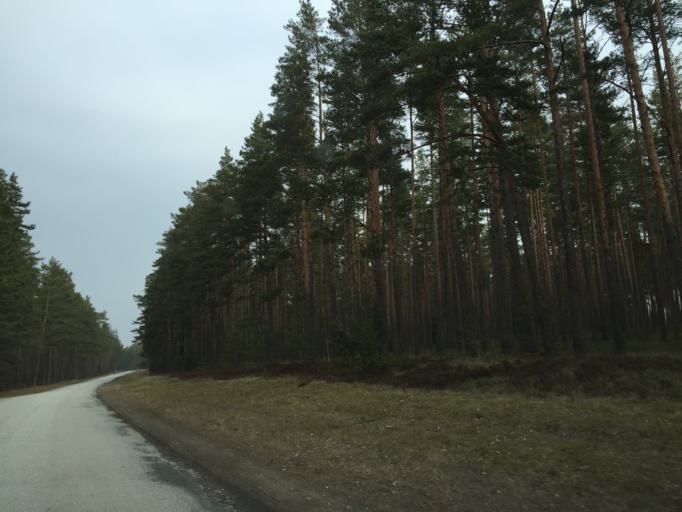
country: LV
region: Salacgrivas
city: Ainazi
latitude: 57.9691
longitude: 24.4086
